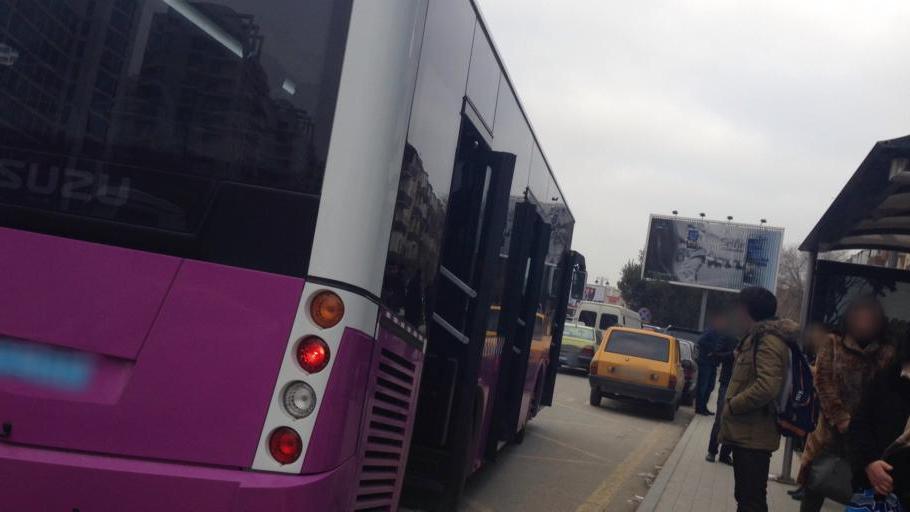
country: AZ
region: Baki
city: Bilajari
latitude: 40.3951
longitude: 49.8174
